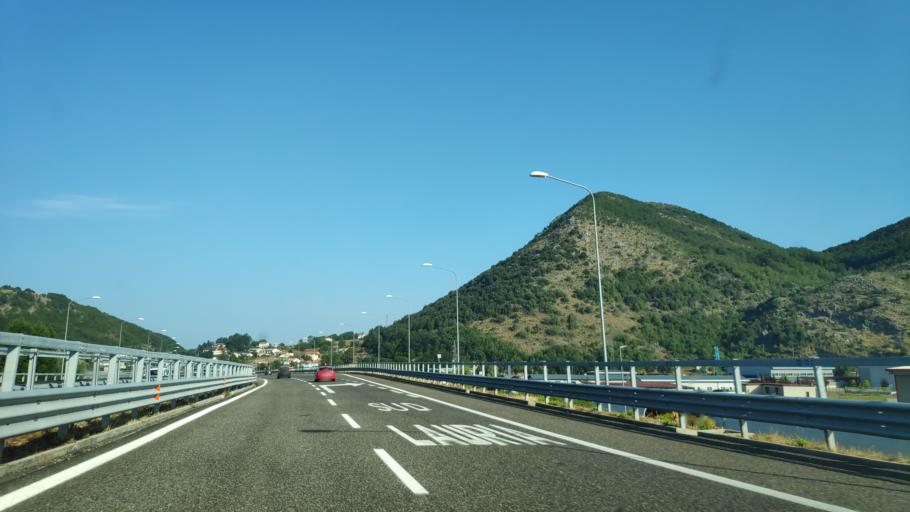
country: IT
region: Basilicate
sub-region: Provincia di Potenza
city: Lauria
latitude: 40.0163
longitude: 15.8929
